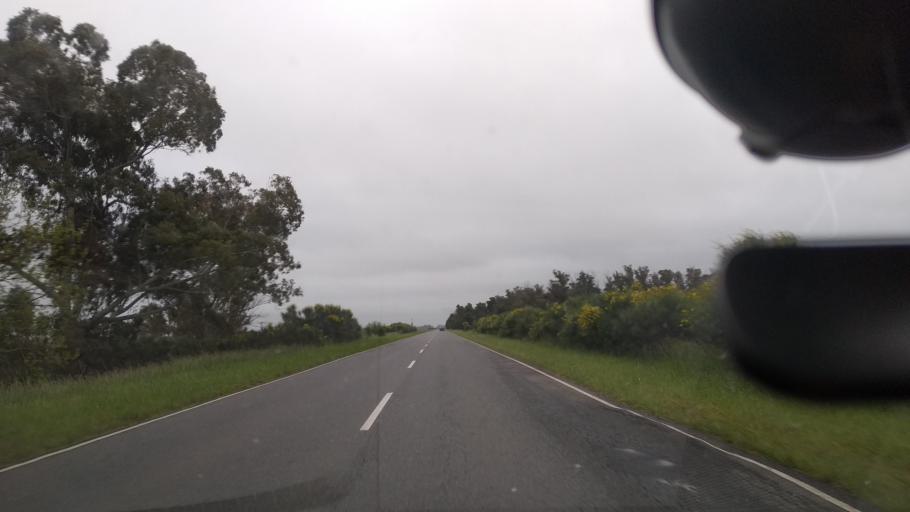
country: AR
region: Buenos Aires
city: Veronica
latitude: -35.4550
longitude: -57.3328
